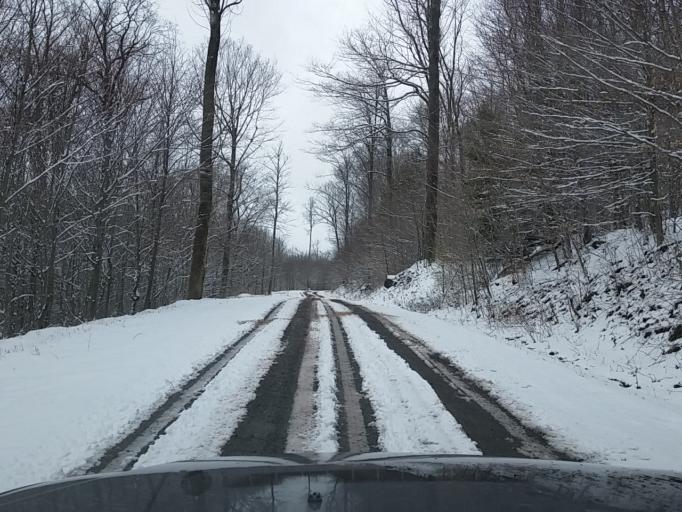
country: US
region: Pennsylvania
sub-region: Sullivan County
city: Laporte
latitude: 41.3403
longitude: -76.4625
